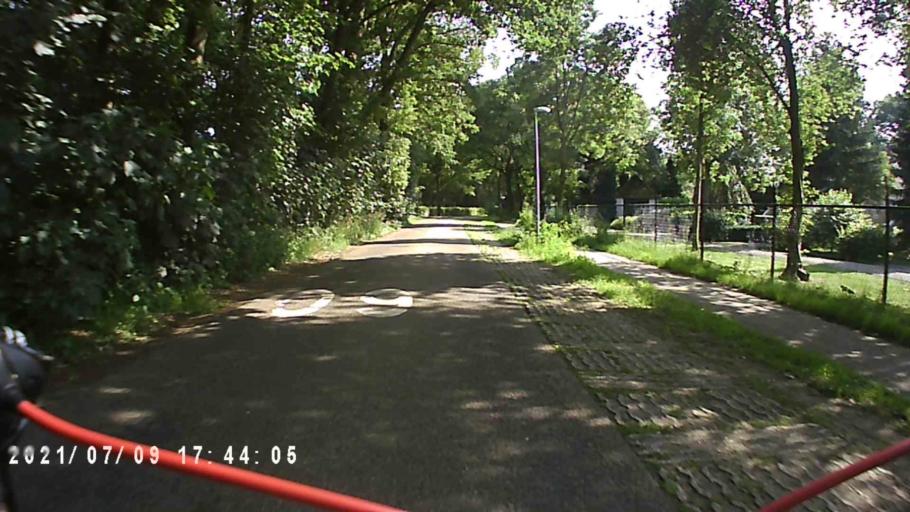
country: NL
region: Groningen
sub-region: Gemeente Vlagtwedde
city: Vlagtwedde
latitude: 53.0850
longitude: 7.0792
